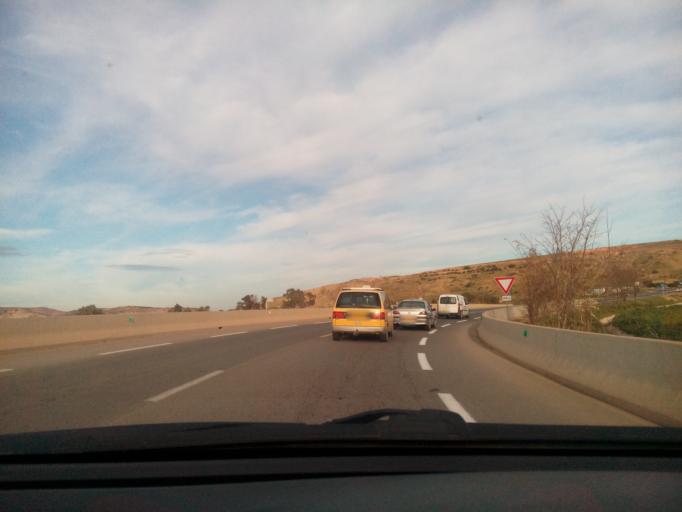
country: DZ
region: Tlemcen
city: Nedroma
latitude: 34.9079
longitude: -1.6431
